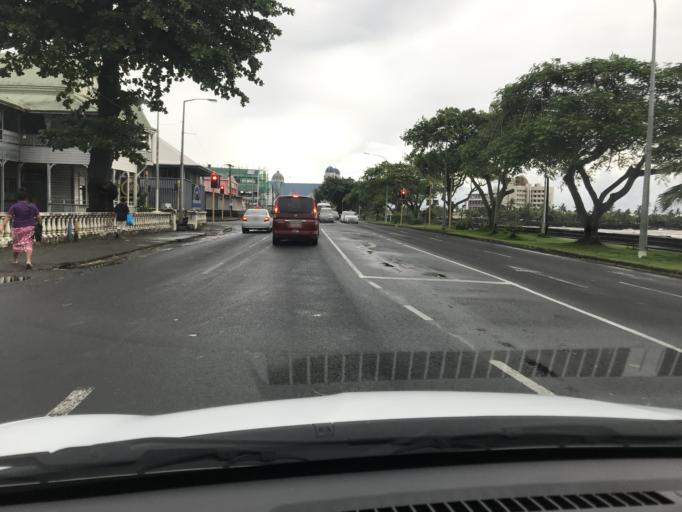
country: WS
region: Tuamasaga
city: Apia
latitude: -13.8332
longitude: -171.7631
